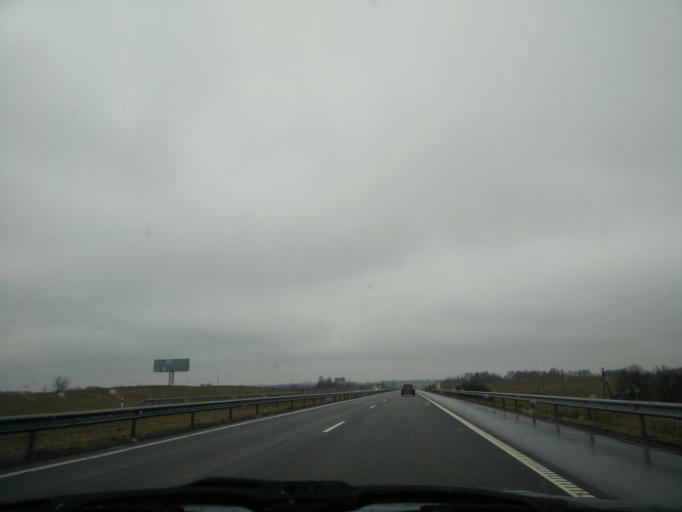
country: LT
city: Skaudvile
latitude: 55.4714
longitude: 22.6461
